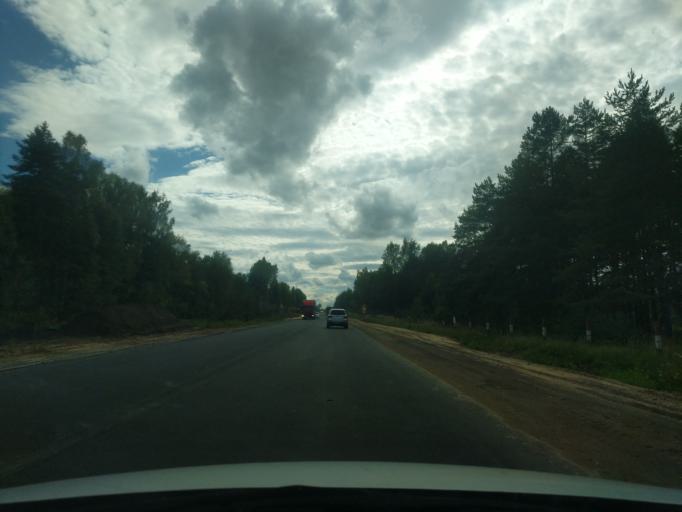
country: RU
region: Jaroslavl
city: Levashevo
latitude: 57.6665
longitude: 40.5752
